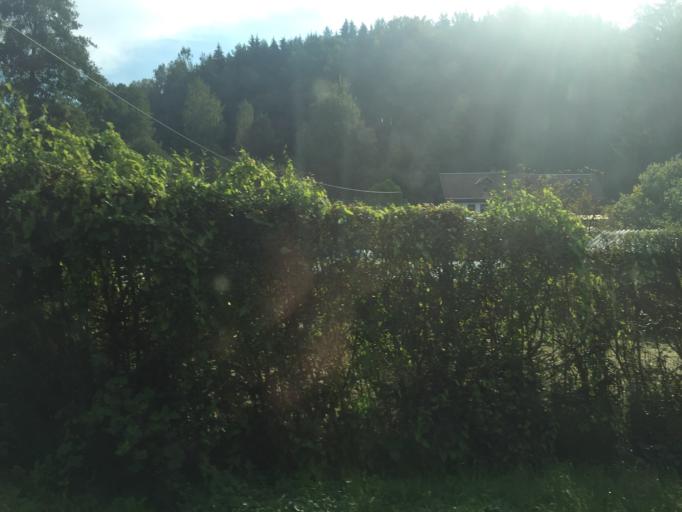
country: CZ
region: Ustecky
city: Ceska Kamenice
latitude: 50.8320
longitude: 14.3578
